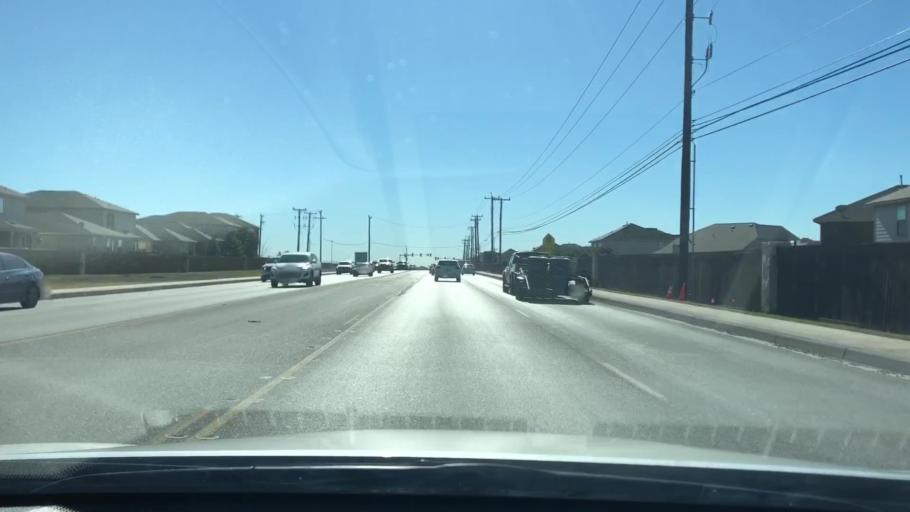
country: US
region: Texas
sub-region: Bexar County
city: Kirby
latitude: 29.4607
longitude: -98.3595
